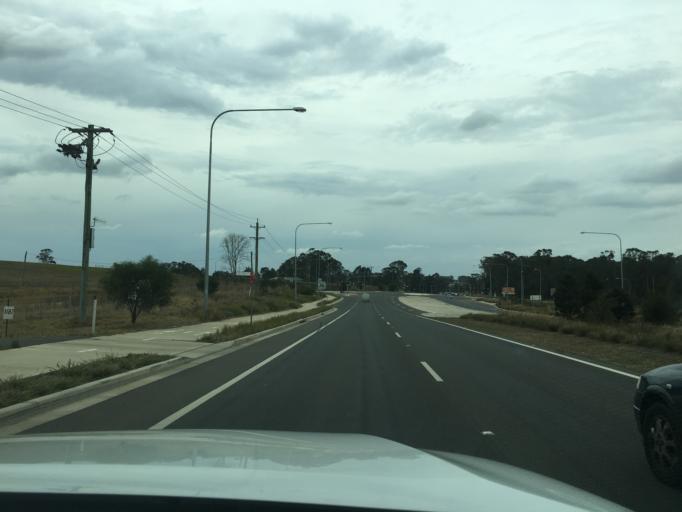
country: AU
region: New South Wales
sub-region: Campbelltown Municipality
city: Denham Court
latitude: -33.9837
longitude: 150.7970
